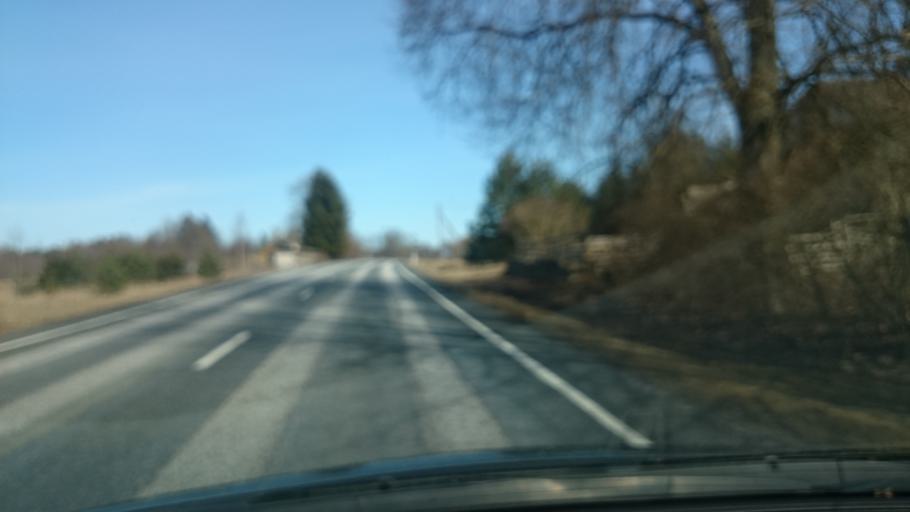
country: EE
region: Jaervamaa
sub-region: Tueri vald
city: Sarevere
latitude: 58.7494
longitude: 25.3185
